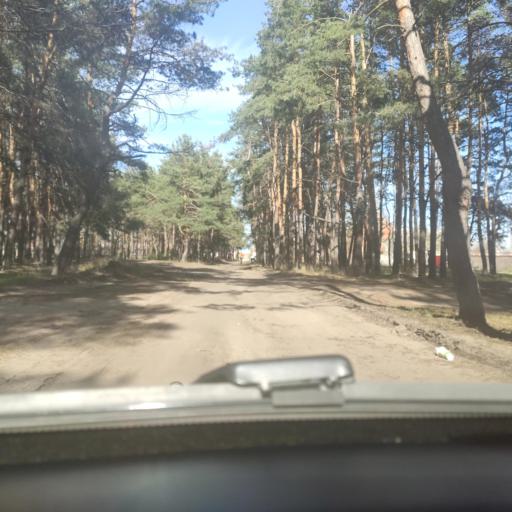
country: RU
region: Voronezj
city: Somovo
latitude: 51.7476
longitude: 39.3241
